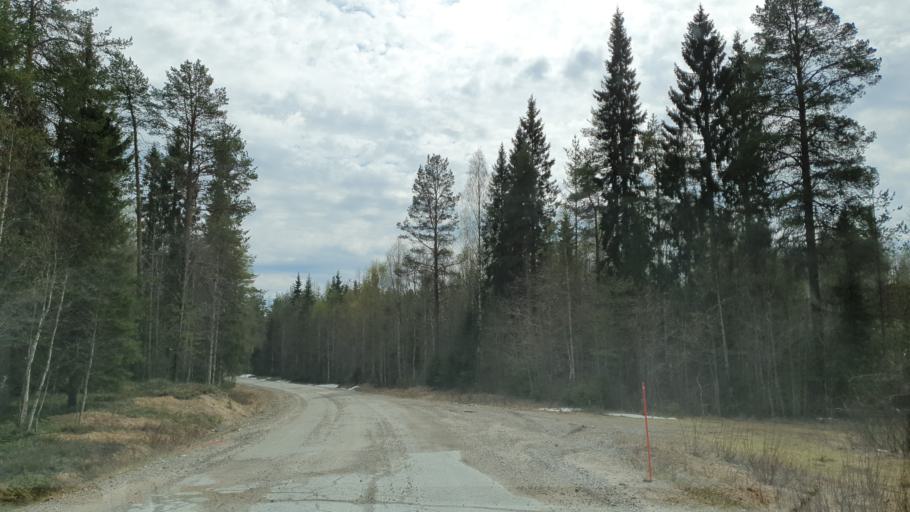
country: FI
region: Kainuu
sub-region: Kehys-Kainuu
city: Kuhmo
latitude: 64.1210
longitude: 29.9536
